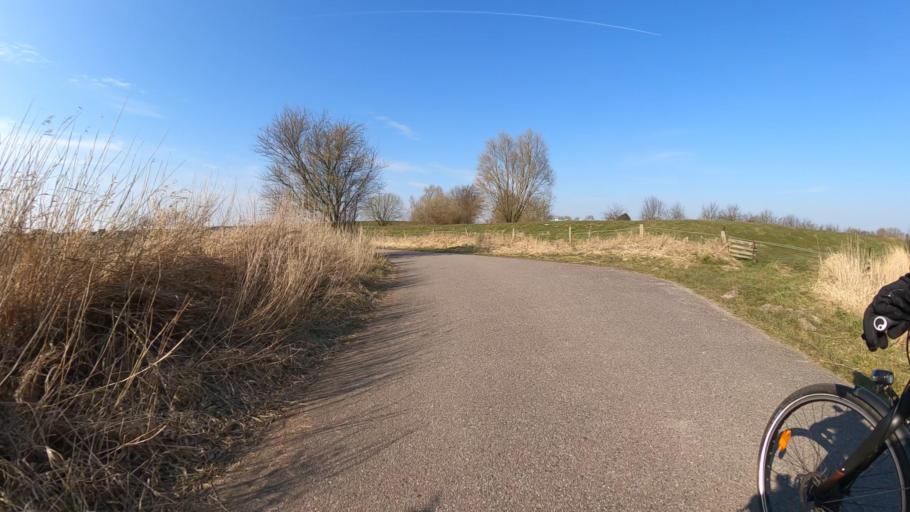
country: DE
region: Schleswig-Holstein
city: Seestermuhe
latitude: 53.7135
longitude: 9.5286
